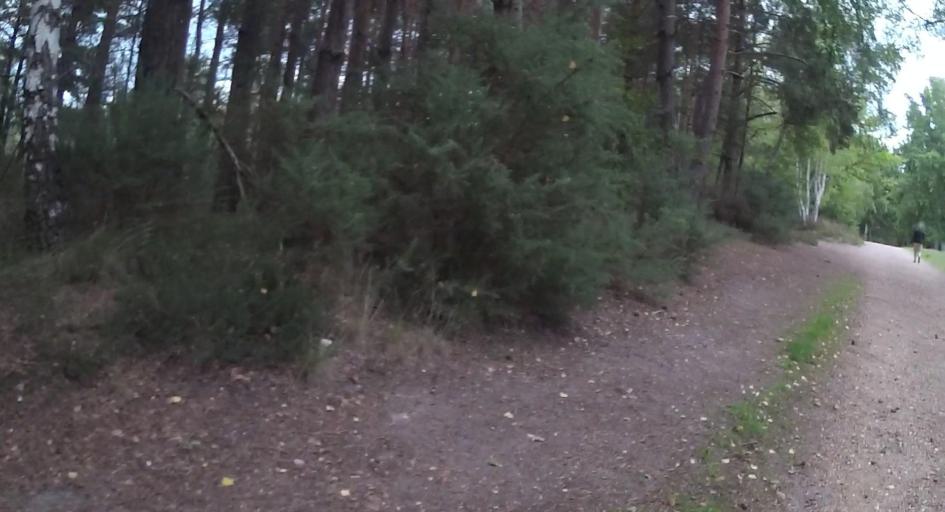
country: GB
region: England
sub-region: Surrey
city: Windlesham
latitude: 51.3424
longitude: -0.6654
